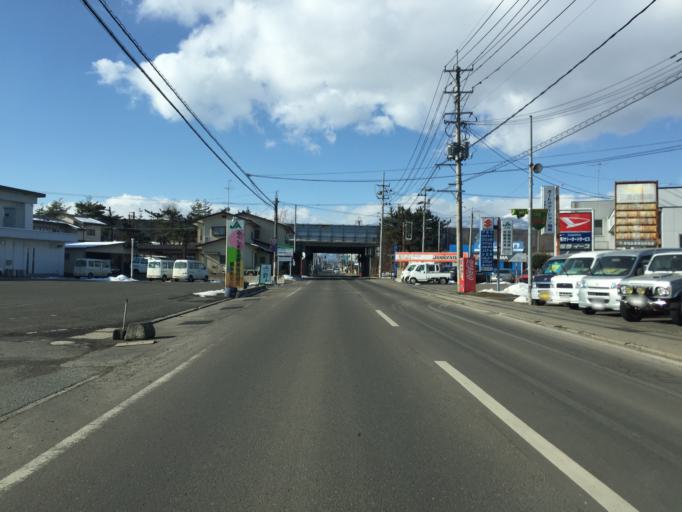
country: JP
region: Fukushima
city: Fukushima-shi
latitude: 37.7415
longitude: 140.4197
